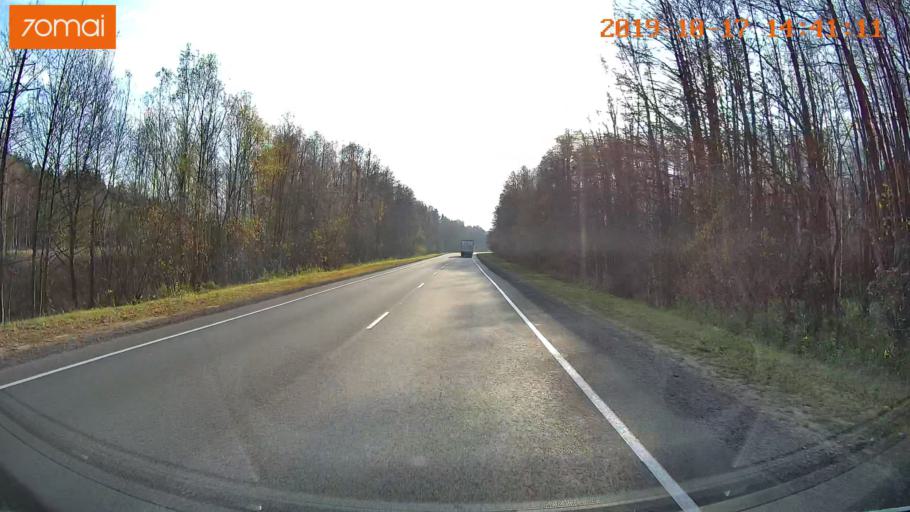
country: RU
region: Rjazan
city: Solotcha
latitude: 54.8481
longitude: 39.9427
